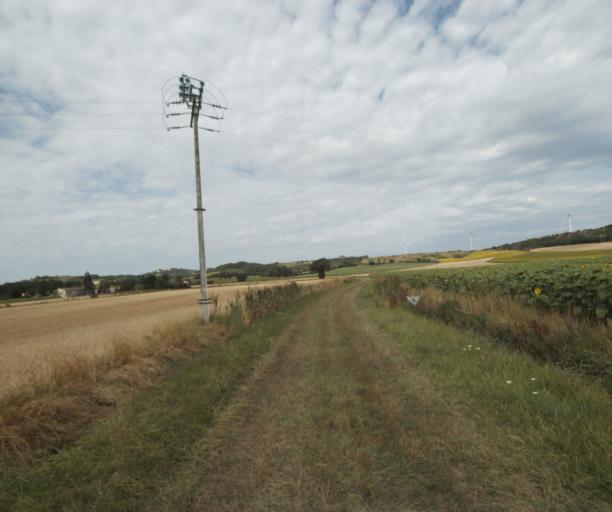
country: FR
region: Midi-Pyrenees
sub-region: Departement de la Haute-Garonne
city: Saint-Felix-Lauragais
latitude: 43.4519
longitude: 1.9210
